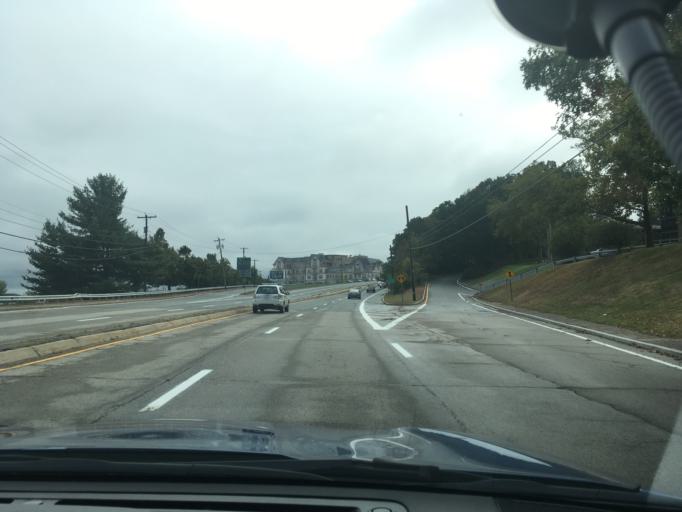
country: US
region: Rhode Island
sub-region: Providence County
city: Cranston
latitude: 41.7611
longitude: -71.4596
